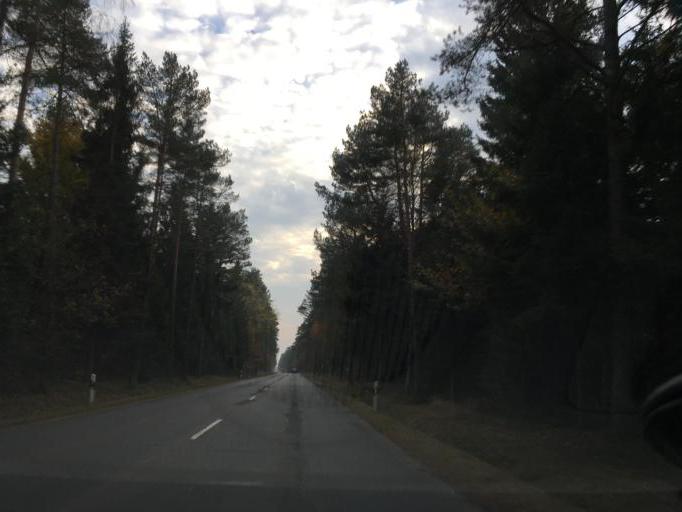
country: DE
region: Lower Saxony
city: Wietzendorf
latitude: 52.9796
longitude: 9.9844
